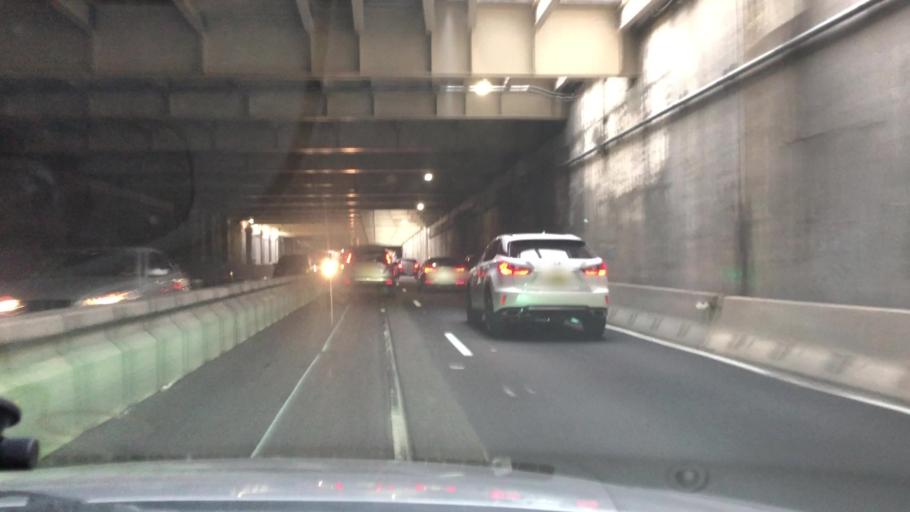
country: US
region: New Jersey
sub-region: Hudson County
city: Hoboken
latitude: 40.7327
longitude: -74.0536
